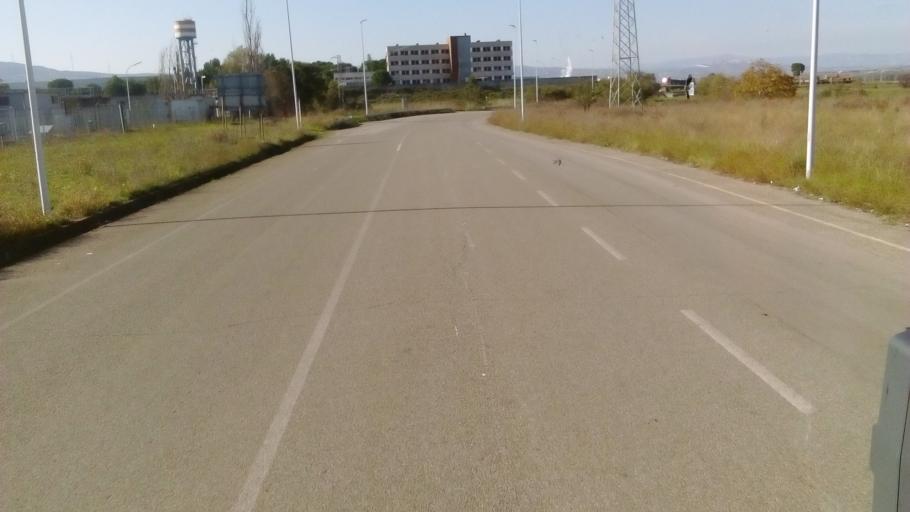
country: IT
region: Basilicate
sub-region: Provincia di Potenza
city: Melfi
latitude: 41.0764
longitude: 15.6773
